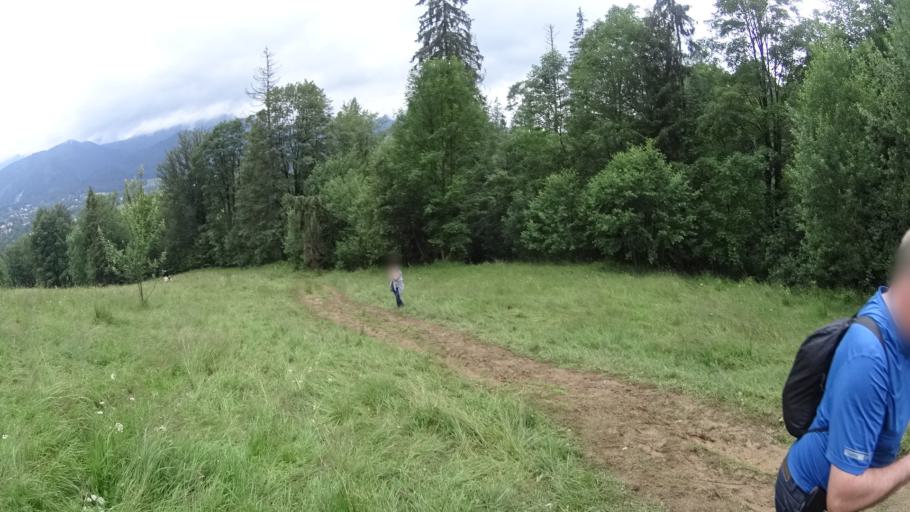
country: PL
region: Lesser Poland Voivodeship
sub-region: Powiat tatrzanski
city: Zakopane
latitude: 49.3019
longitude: 19.9406
